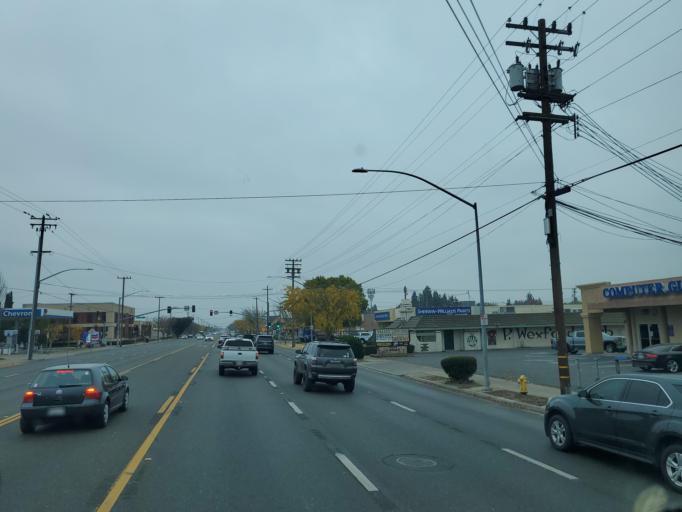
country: US
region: California
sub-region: Stanislaus County
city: Modesto
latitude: 37.6864
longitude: -120.9944
